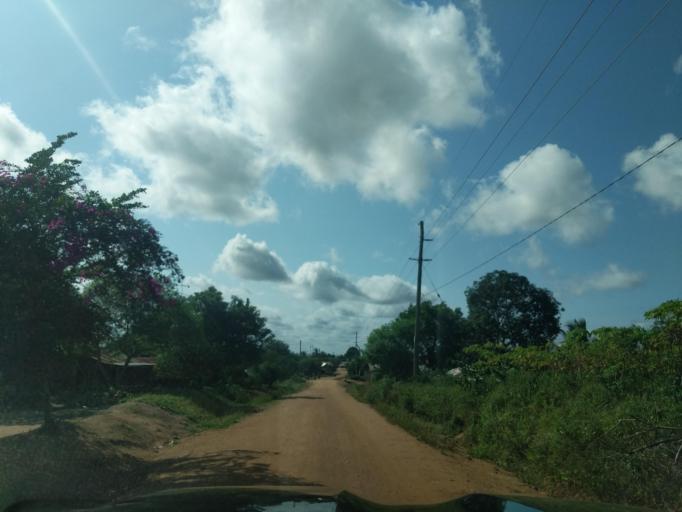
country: TZ
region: Tanga
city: Muheza
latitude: -5.4216
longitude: 38.6328
